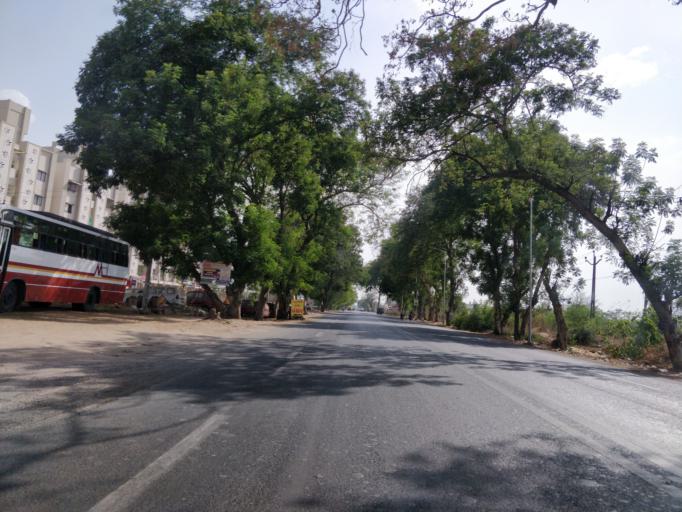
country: IN
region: Gujarat
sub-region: Ahmadabad
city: Naroda
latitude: 23.0844
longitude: 72.6783
